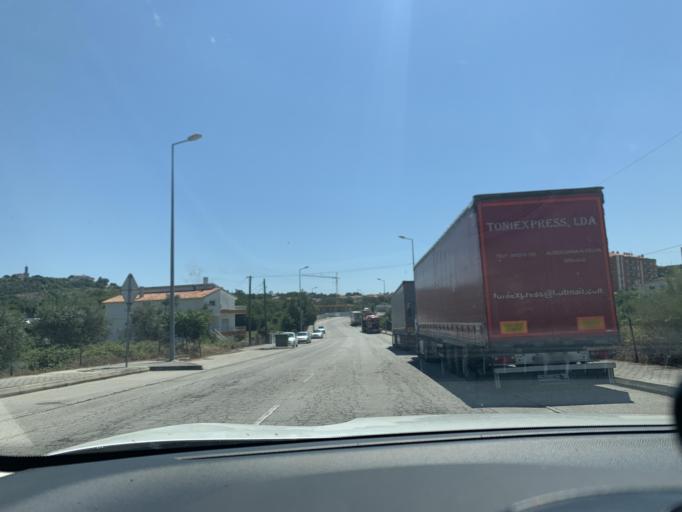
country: PT
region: Viseu
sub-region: Mangualde
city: Mangualde
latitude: 40.6093
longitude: -7.7603
